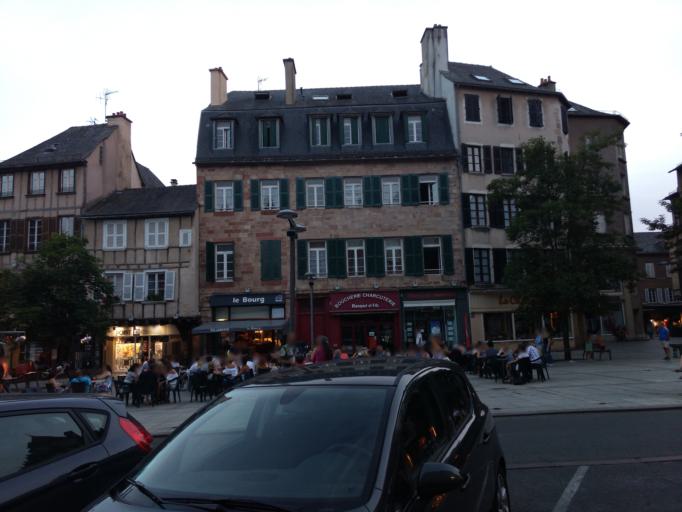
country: FR
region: Midi-Pyrenees
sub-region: Departement de l'Aveyron
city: Rodez
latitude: 44.3489
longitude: 2.5757
